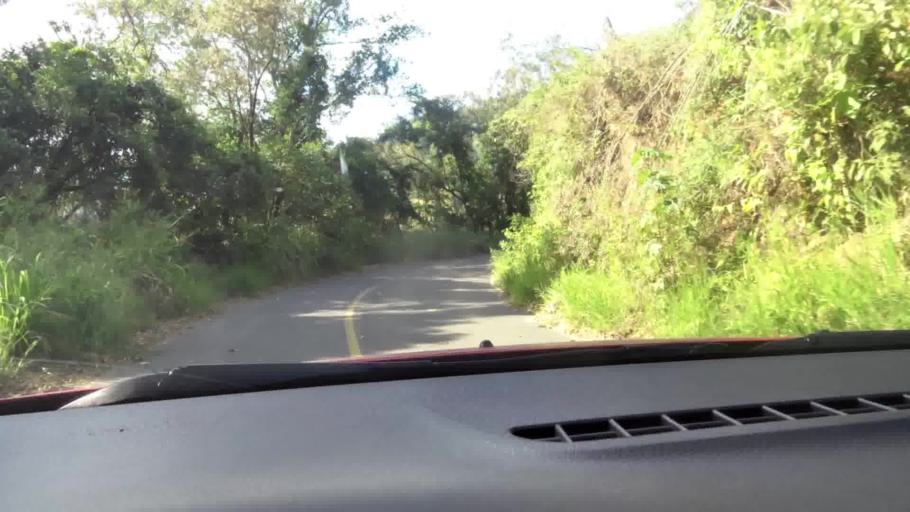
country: BR
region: Espirito Santo
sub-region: Guarapari
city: Guarapari
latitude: -20.5792
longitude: -40.5494
